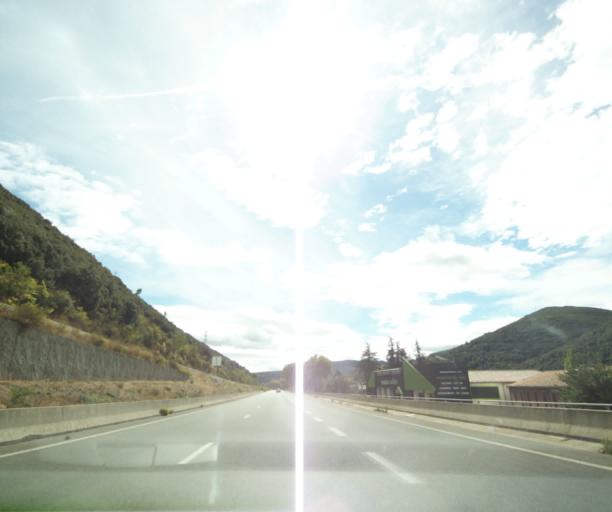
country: FR
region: Languedoc-Roussillon
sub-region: Departement de l'Herault
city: Lodeve
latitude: 43.7202
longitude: 3.3244
